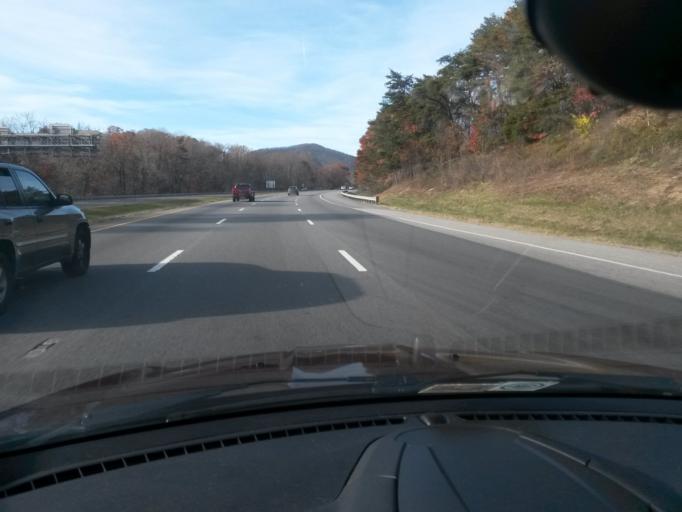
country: US
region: Virginia
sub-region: Roanoke County
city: Hollins
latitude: 37.3306
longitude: -79.9923
